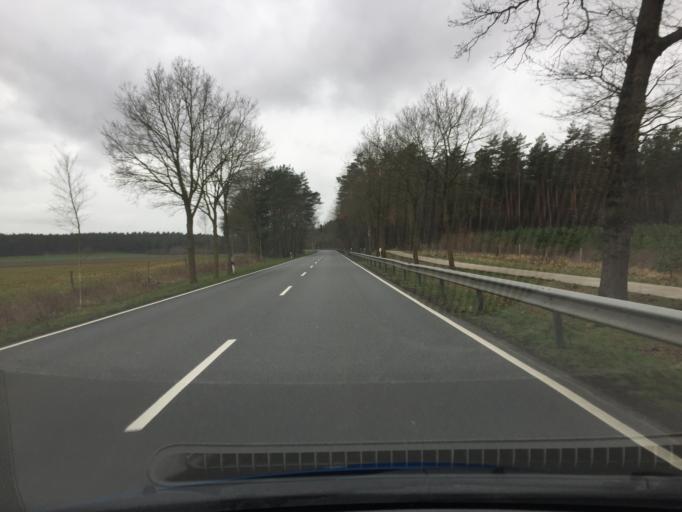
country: DE
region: Lower Saxony
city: Stoetze
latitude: 53.0421
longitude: 10.7951
